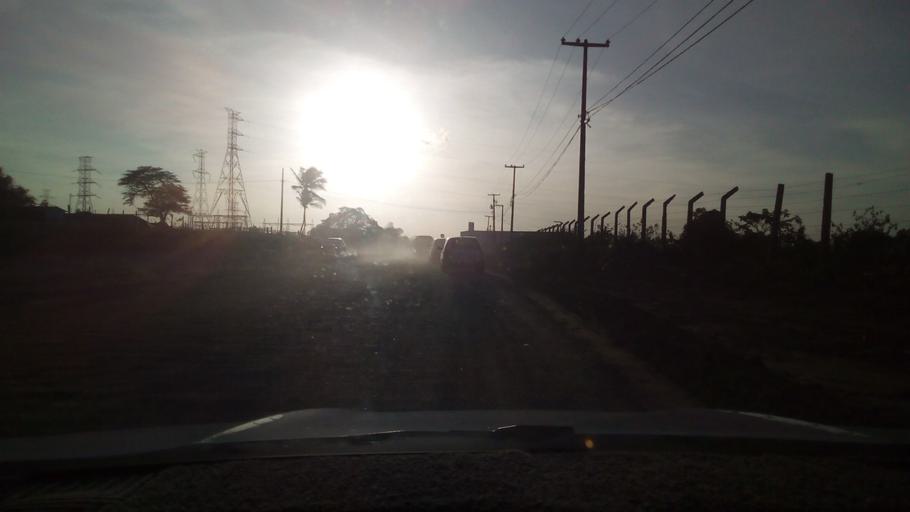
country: BR
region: Paraiba
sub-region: Conde
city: Conde
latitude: -7.1948
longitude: -34.8962
